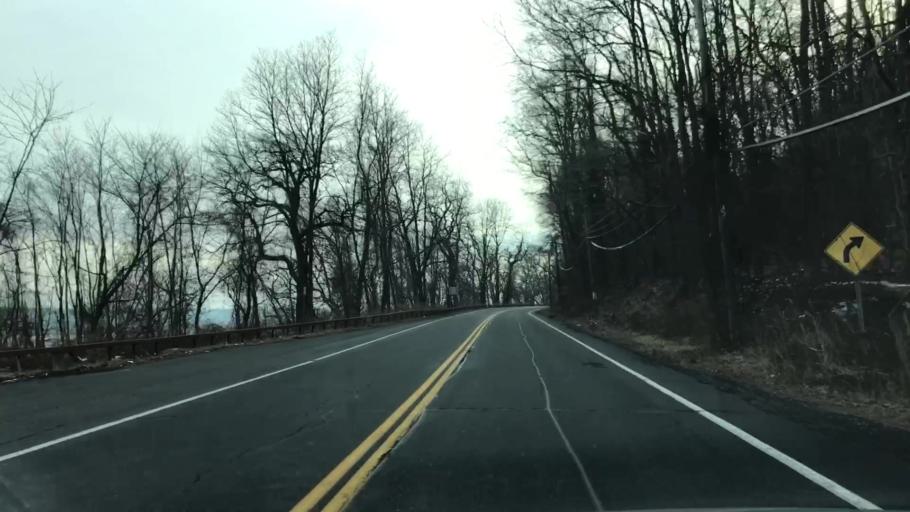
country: US
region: New York
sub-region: Rockland County
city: Haverstraw
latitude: 41.1793
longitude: -73.9491
